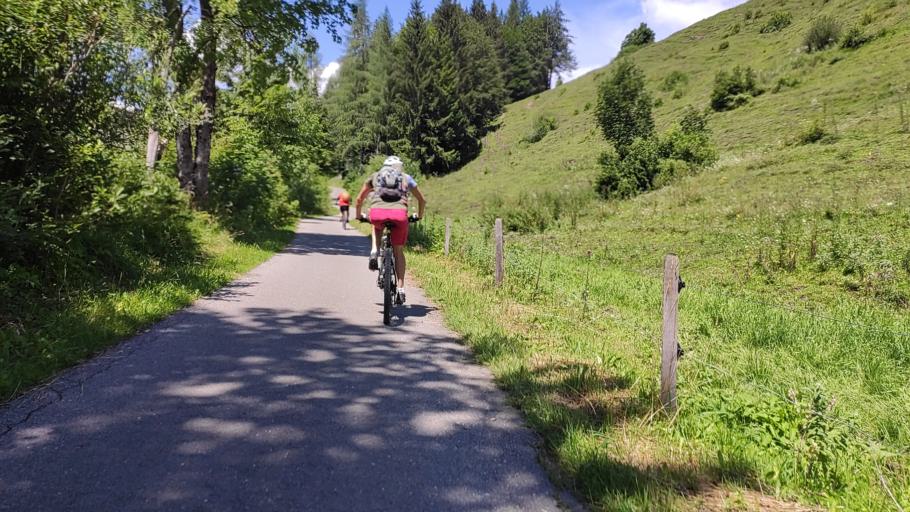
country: AT
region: Tyrol
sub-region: Politischer Bezirk Kitzbuhel
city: Hochfilzen
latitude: 47.4675
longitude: 12.6353
